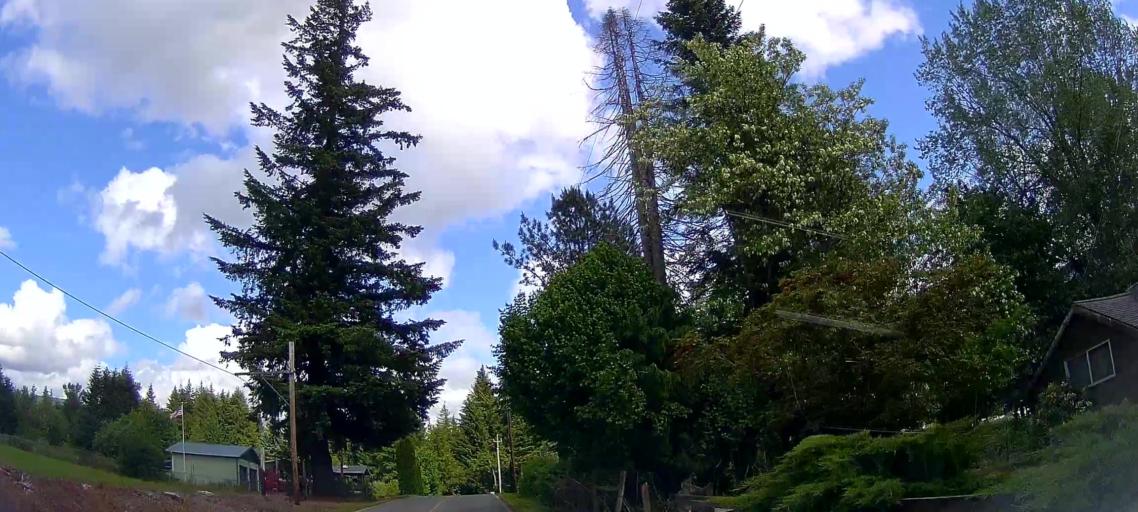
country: US
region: Washington
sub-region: Whatcom County
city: Sudden Valley
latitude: 48.6785
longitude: -122.1884
